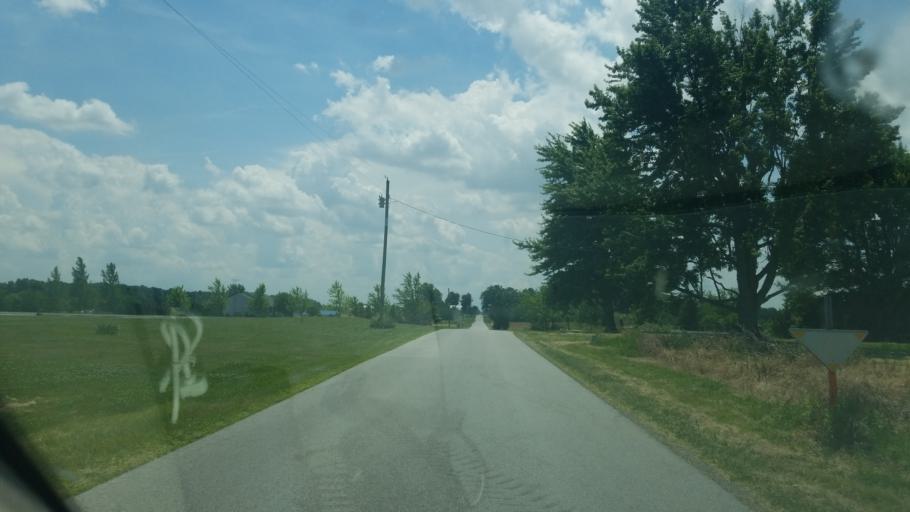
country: US
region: Ohio
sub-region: Hancock County
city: Arlington
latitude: 40.8695
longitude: -83.5998
